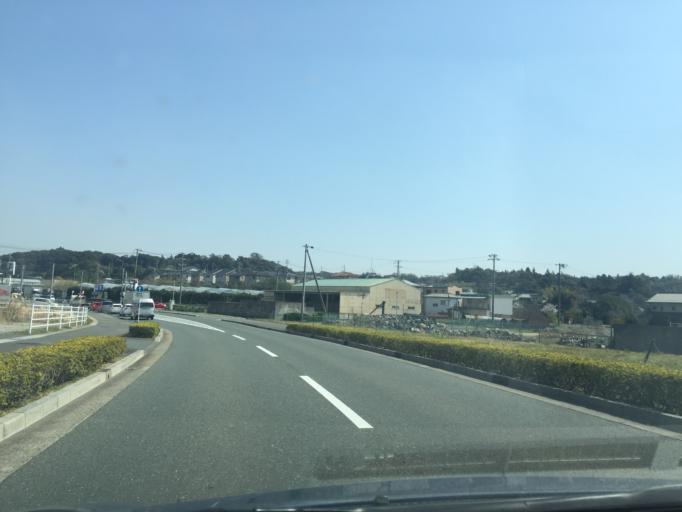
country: JP
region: Shizuoka
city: Hamamatsu
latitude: 34.7937
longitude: 137.6466
